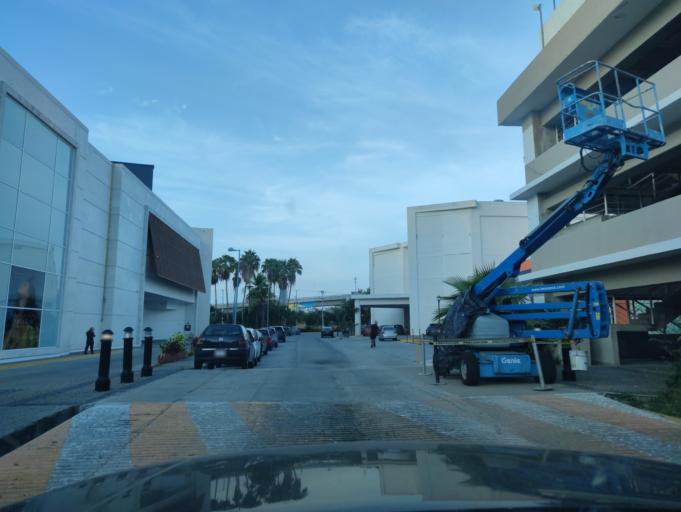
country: MX
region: Guerrero
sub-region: Acapulco de Juarez
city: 10 de Abril
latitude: 16.7717
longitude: -99.7750
